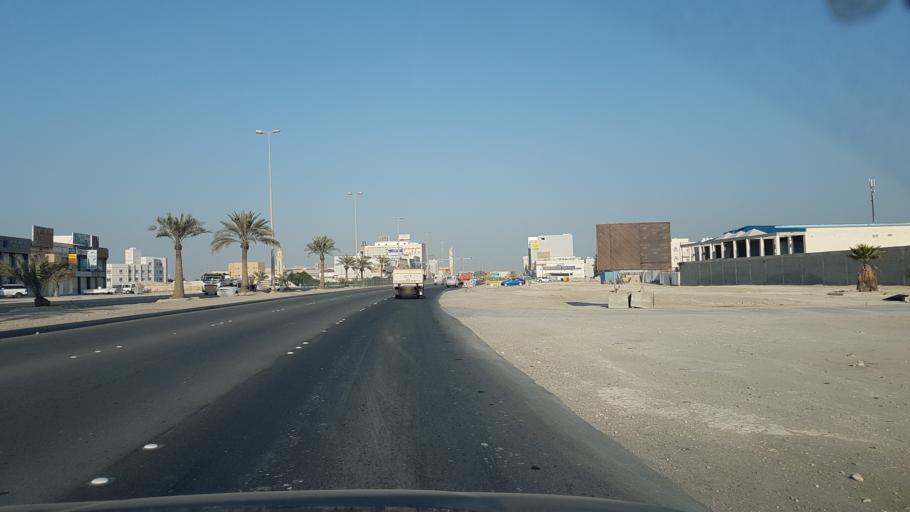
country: BH
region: Northern
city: Sitrah
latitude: 26.1370
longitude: 50.6083
